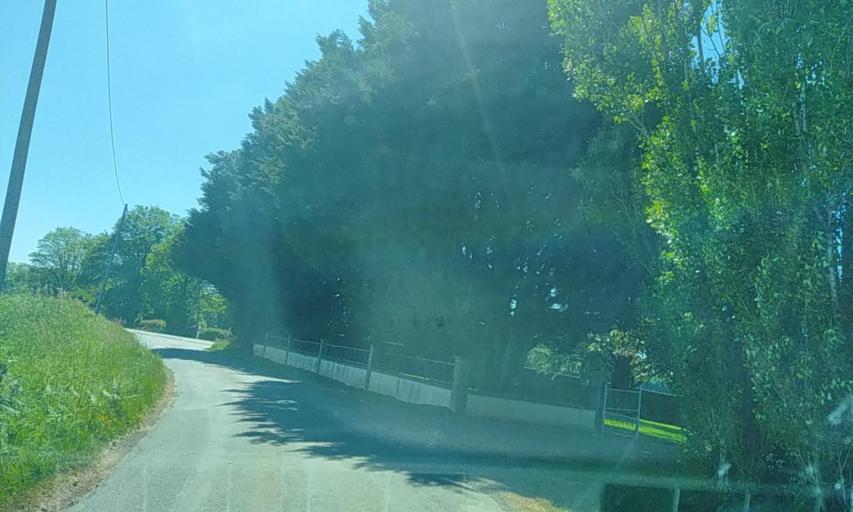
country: FR
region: Poitou-Charentes
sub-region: Departement des Deux-Sevres
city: La Chapelle-Saint-Laurent
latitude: 46.7814
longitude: -0.4775
